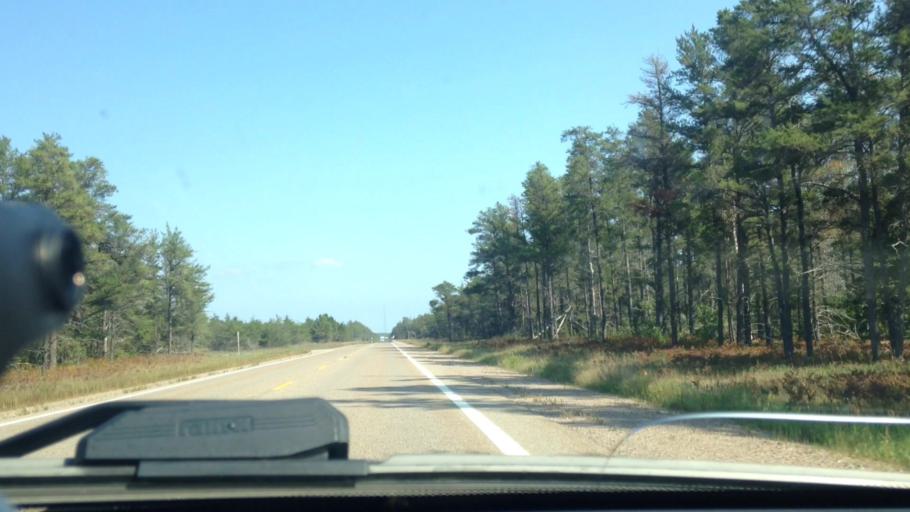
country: US
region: Michigan
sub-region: Mackinac County
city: Saint Ignace
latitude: 46.3586
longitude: -84.8316
